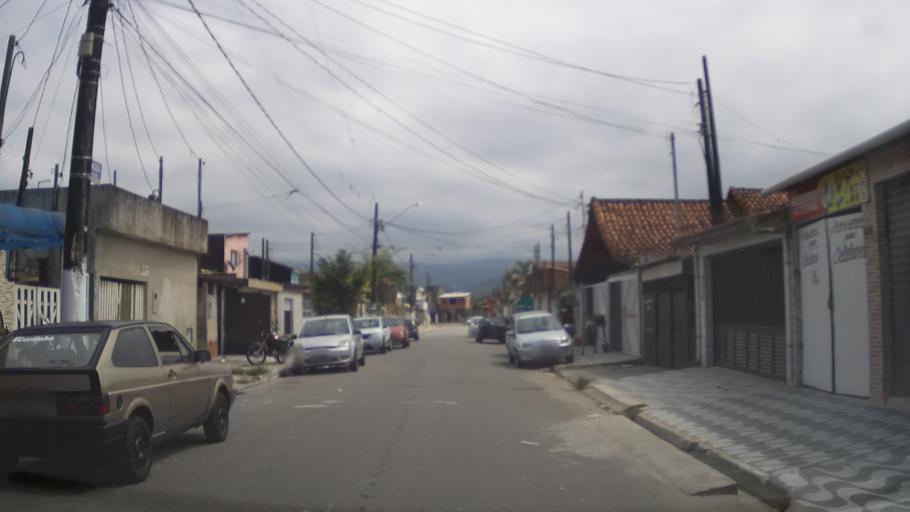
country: BR
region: Sao Paulo
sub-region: Praia Grande
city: Praia Grande
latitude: -24.0199
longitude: -46.4924
